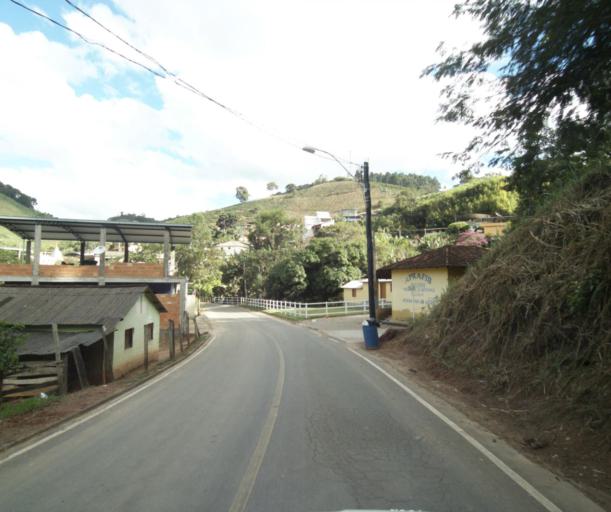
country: BR
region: Espirito Santo
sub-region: Irupi
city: Irupi
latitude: -20.5392
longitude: -41.6685
